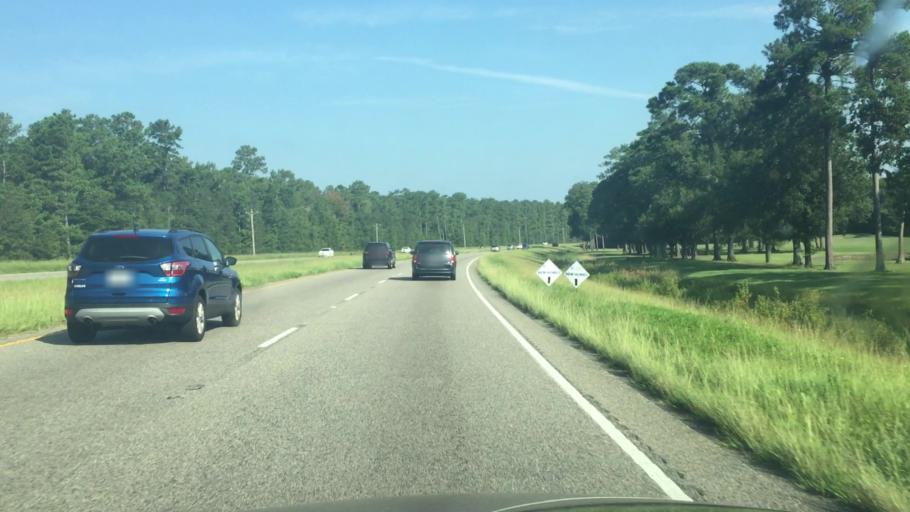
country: US
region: South Carolina
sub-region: Horry County
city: North Myrtle Beach
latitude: 33.9169
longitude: -78.7216
